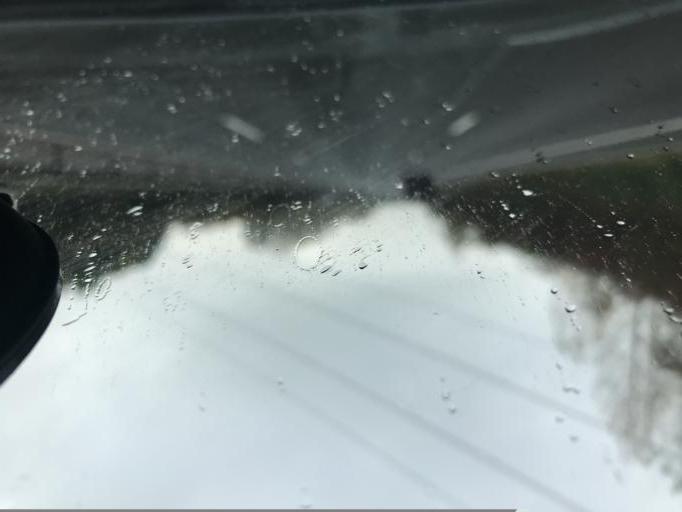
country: GB
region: England
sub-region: Oxfordshire
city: Wheatley
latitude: 51.7570
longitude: -1.1060
